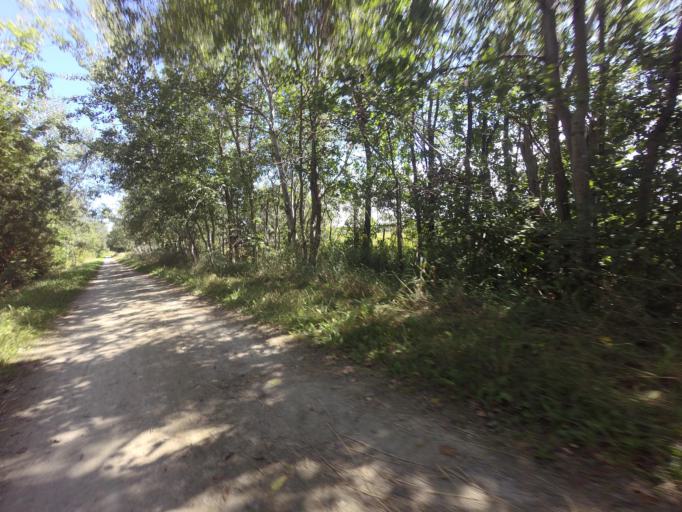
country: CA
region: Ontario
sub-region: Wellington County
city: Guelph
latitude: 43.7368
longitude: -80.3654
